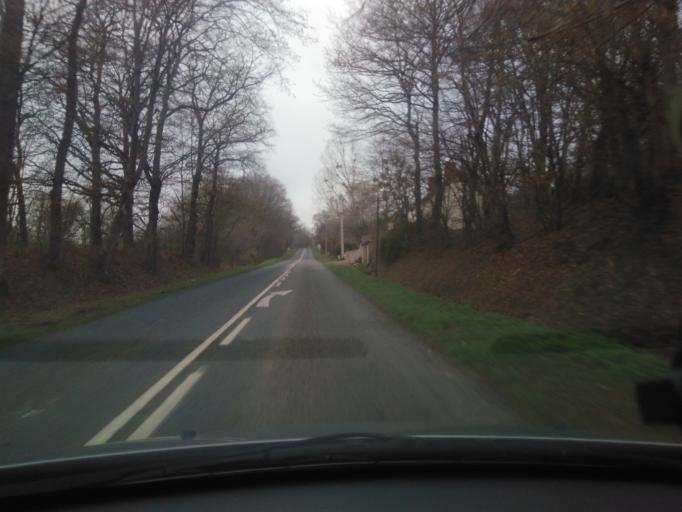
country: FR
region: Centre
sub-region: Departement du Cher
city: Chateaumeillant
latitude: 46.6340
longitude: 2.1713
